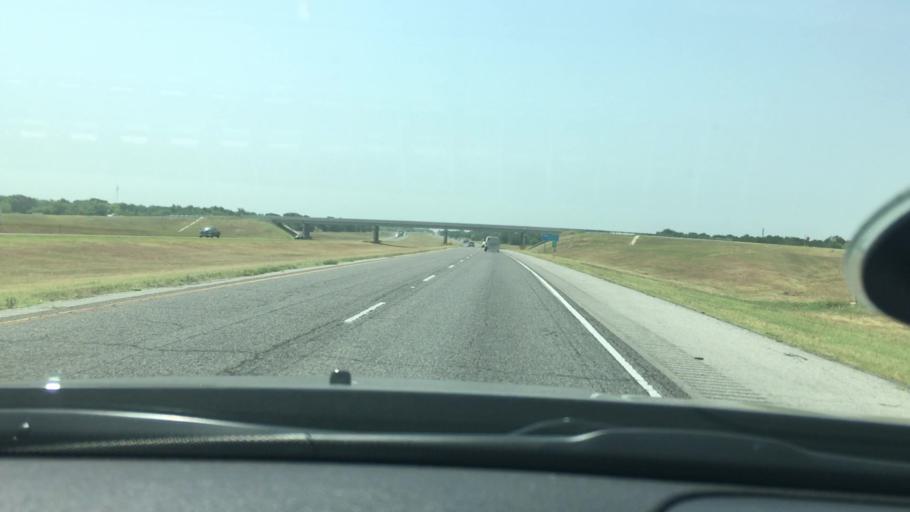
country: US
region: Oklahoma
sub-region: Garvin County
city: Wynnewood
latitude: 34.5744
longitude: -97.2003
